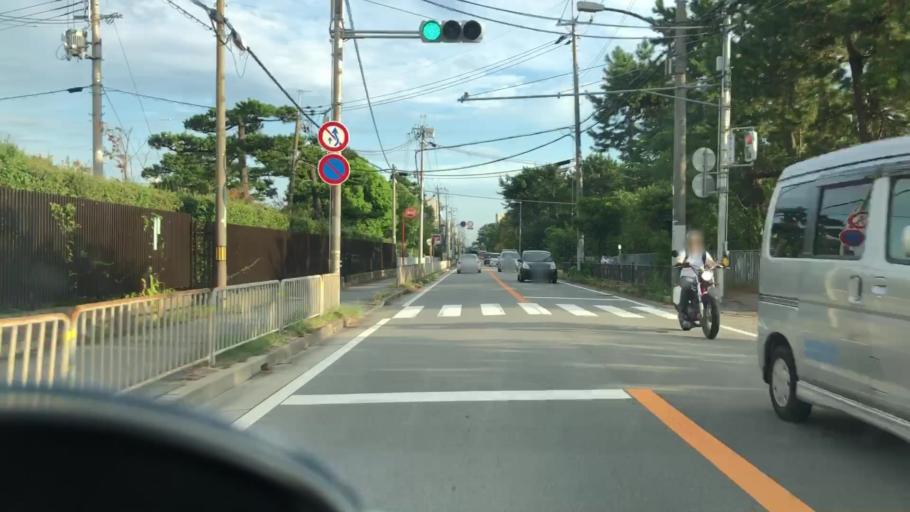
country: JP
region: Hyogo
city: Takarazuka
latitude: 34.7802
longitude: 135.3708
